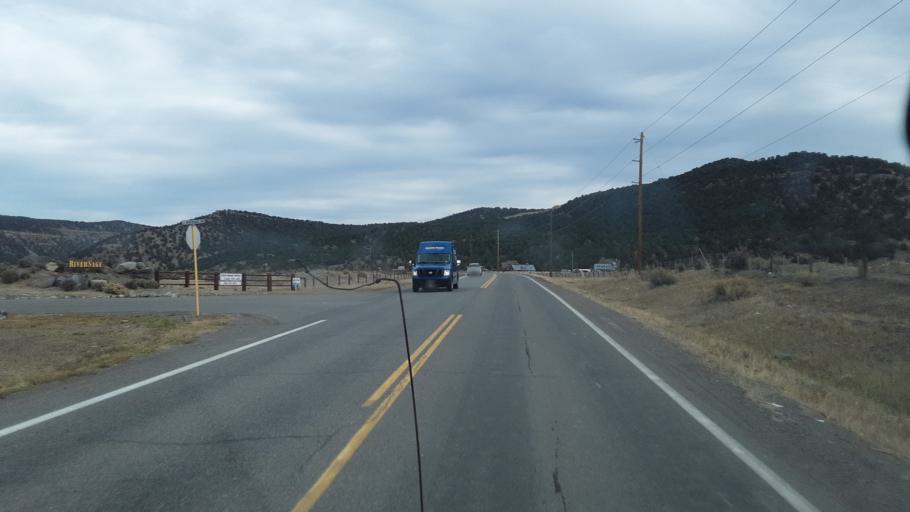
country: US
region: Colorado
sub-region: Ouray County
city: Ouray
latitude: 38.1711
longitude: -107.7429
